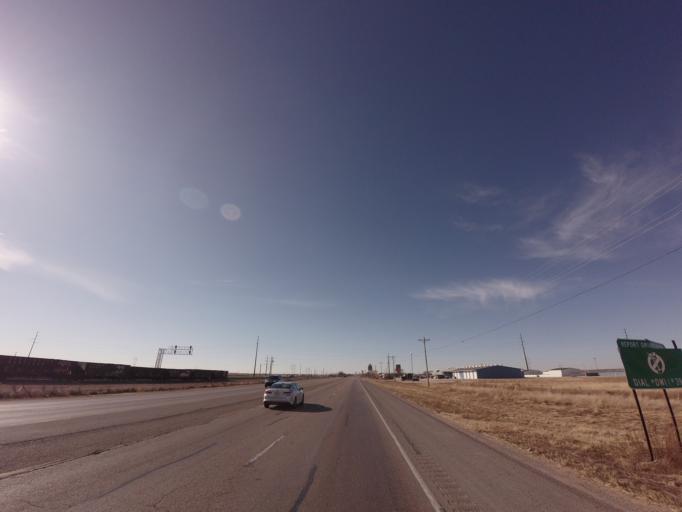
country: US
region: New Mexico
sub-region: Curry County
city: Clovis
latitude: 34.3939
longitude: -103.1395
